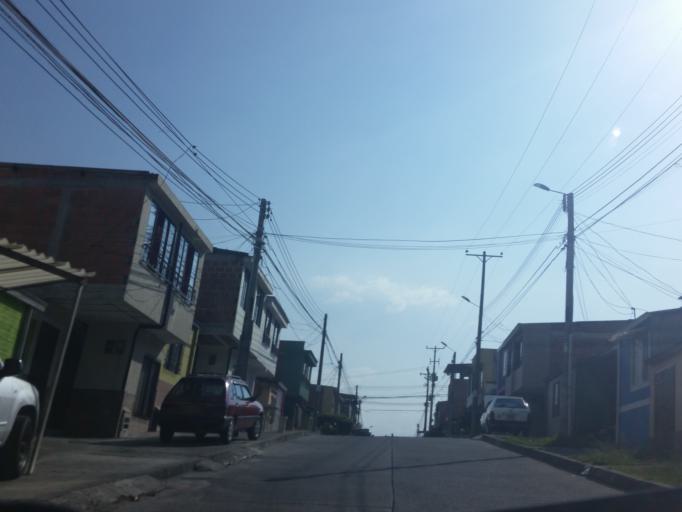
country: CO
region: Caldas
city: Manizales
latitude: 5.0789
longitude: -75.4899
